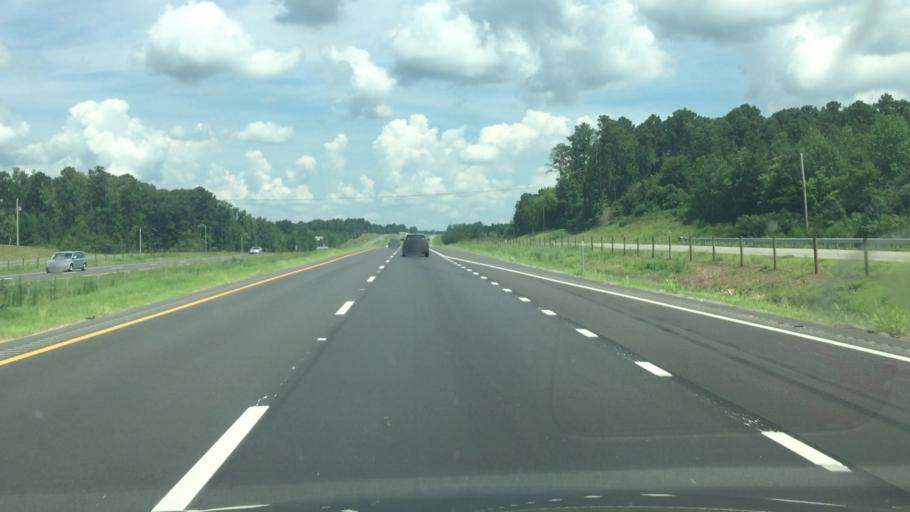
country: US
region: North Carolina
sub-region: Richmond County
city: Ellerbe
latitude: 35.0201
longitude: -79.7698
